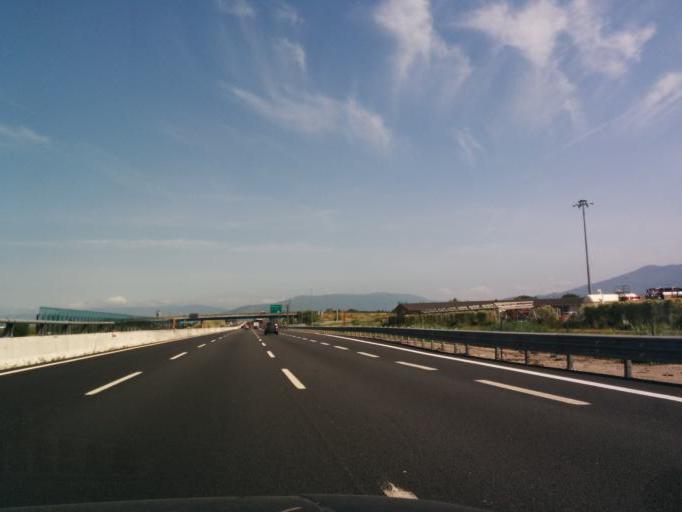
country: IT
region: Tuscany
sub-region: Province of Florence
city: Mantignano-Ugnano
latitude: 43.7745
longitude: 11.1624
